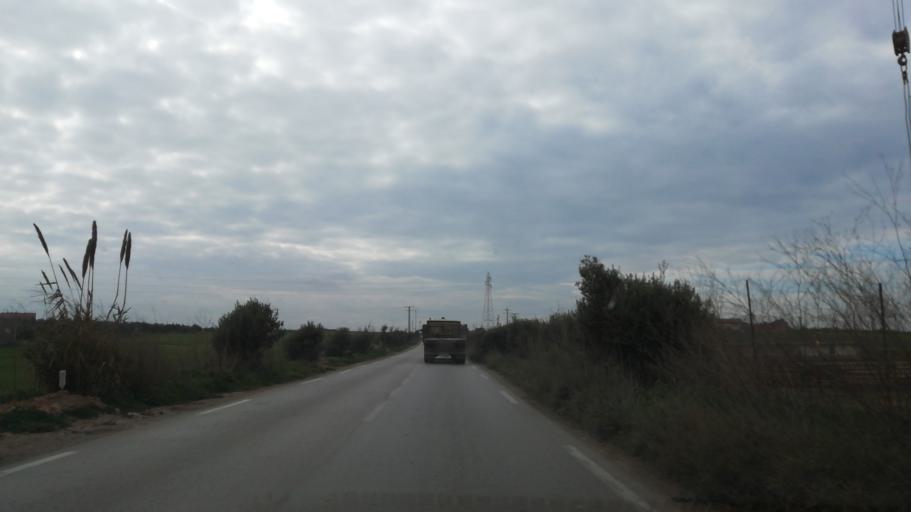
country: DZ
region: Oran
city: Ain el Bya
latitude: 35.7892
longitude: -0.3425
